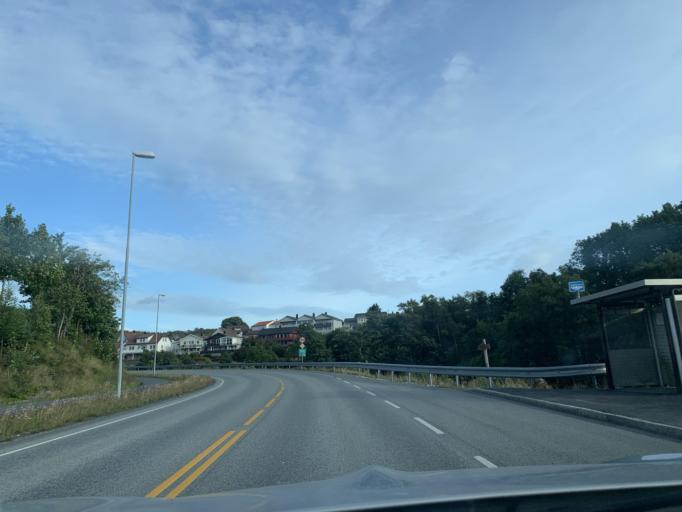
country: NO
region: Rogaland
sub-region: Eigersund
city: Egersund
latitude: 58.4611
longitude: 6.0116
